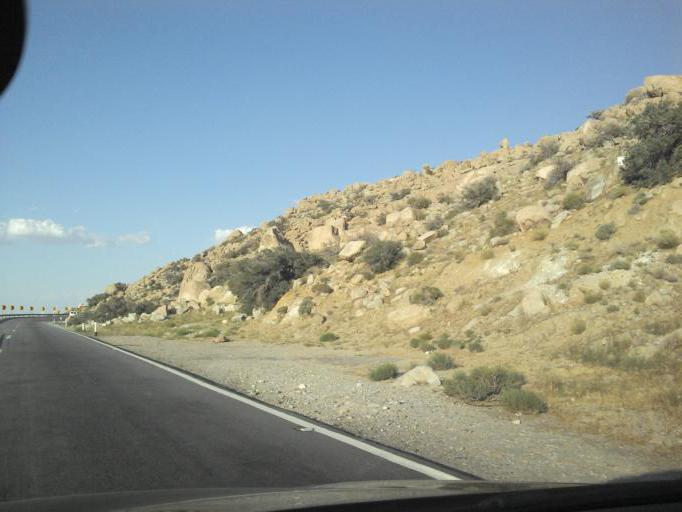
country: MX
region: Baja California
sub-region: Tecate
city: Cereso del Hongo
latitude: 32.5789
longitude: -116.0308
